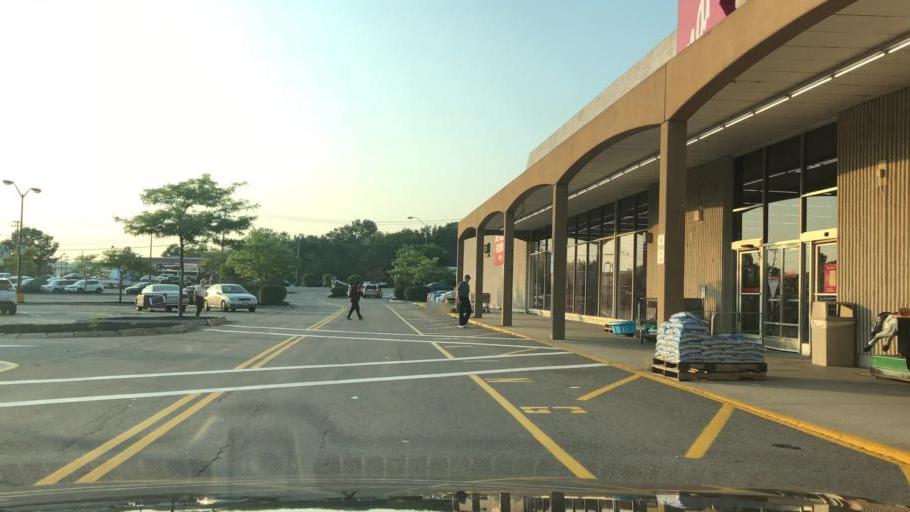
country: US
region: New Hampshire
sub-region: Rockingham County
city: Salem
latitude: 42.7684
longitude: -71.2179
